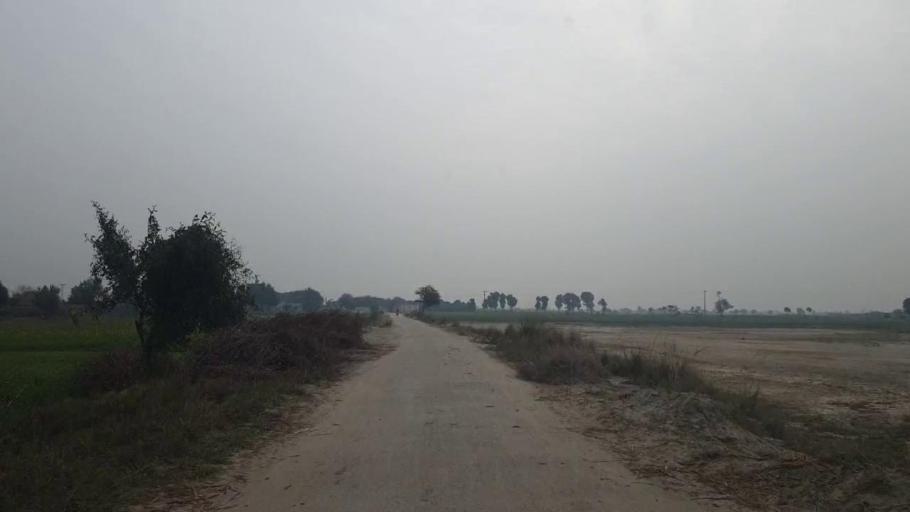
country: PK
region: Sindh
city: Tando Adam
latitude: 25.7502
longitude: 68.6782
